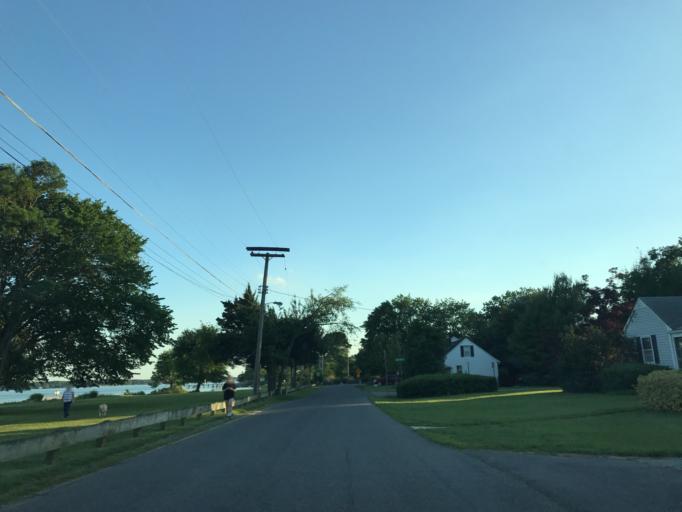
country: US
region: Maryland
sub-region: Anne Arundel County
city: Mayo
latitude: 38.8745
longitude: -76.5057
